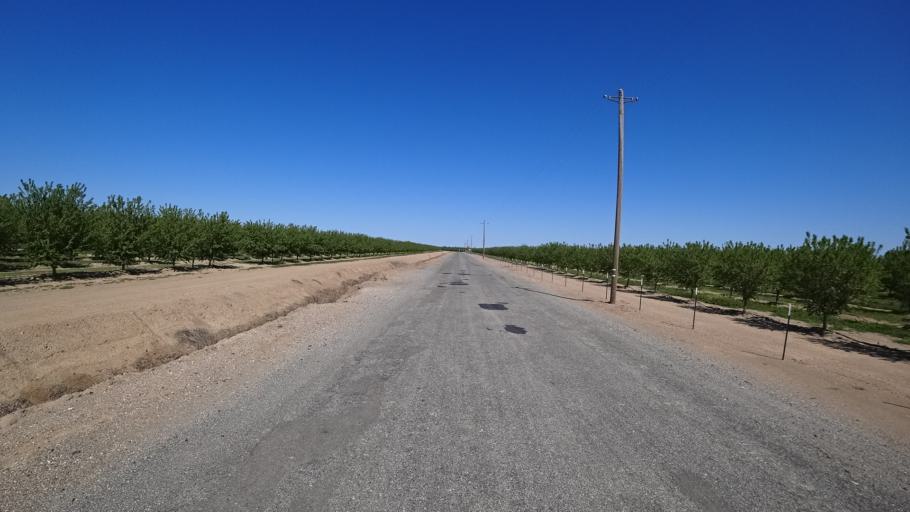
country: US
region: California
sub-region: Glenn County
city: Orland
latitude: 39.6934
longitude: -122.2341
